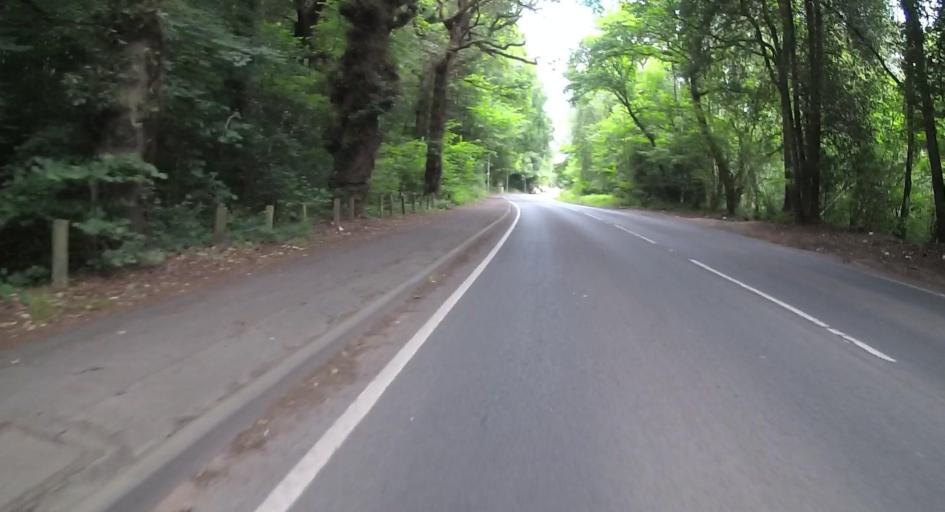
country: GB
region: England
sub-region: Hampshire
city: Fleet
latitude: 51.2554
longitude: -0.8255
